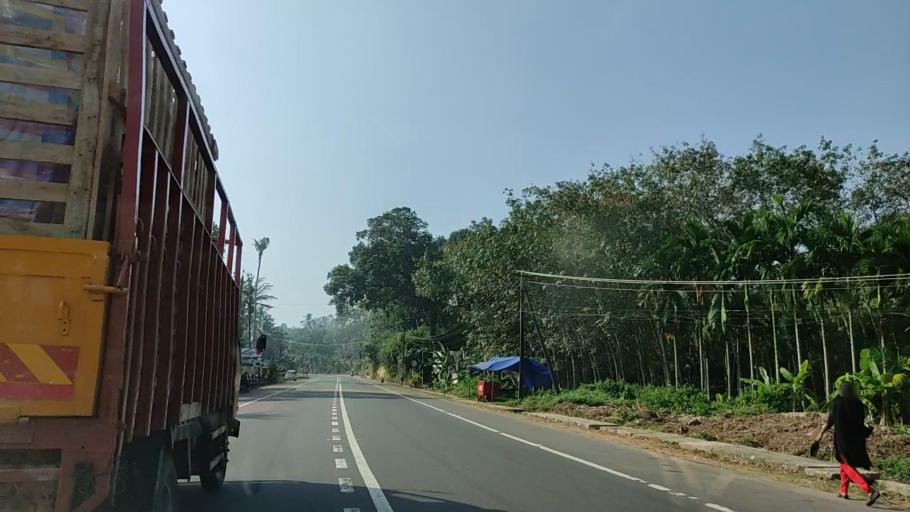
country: IN
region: Kerala
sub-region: Kollam
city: Punalur
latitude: 8.9724
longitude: 76.8286
